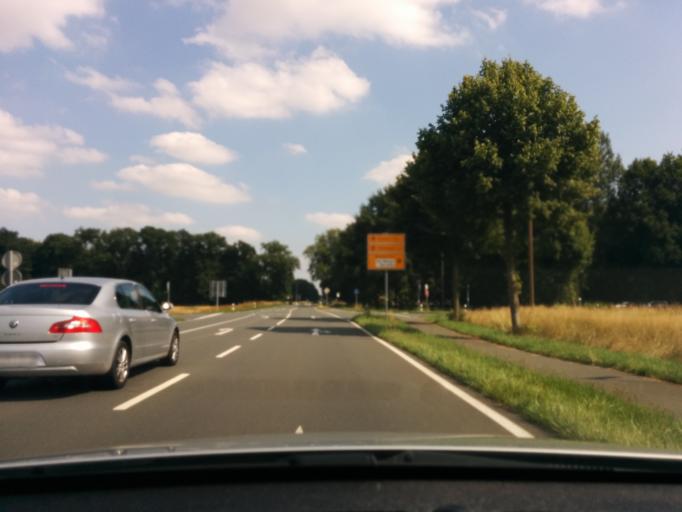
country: DE
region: North Rhine-Westphalia
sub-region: Regierungsbezirk Munster
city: Metelen
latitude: 52.1920
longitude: 7.2515
